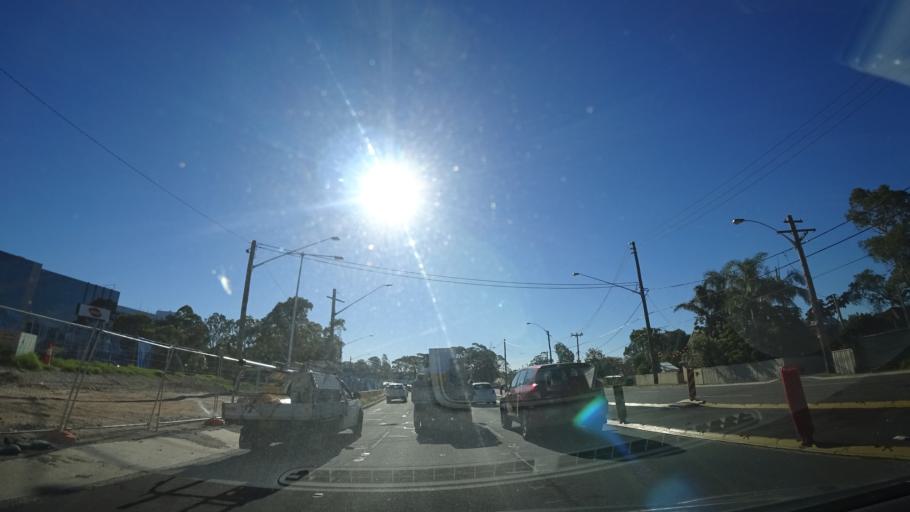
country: AU
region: New South Wales
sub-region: Warringah
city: Allambie Heights
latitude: -33.7518
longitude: 151.2468
